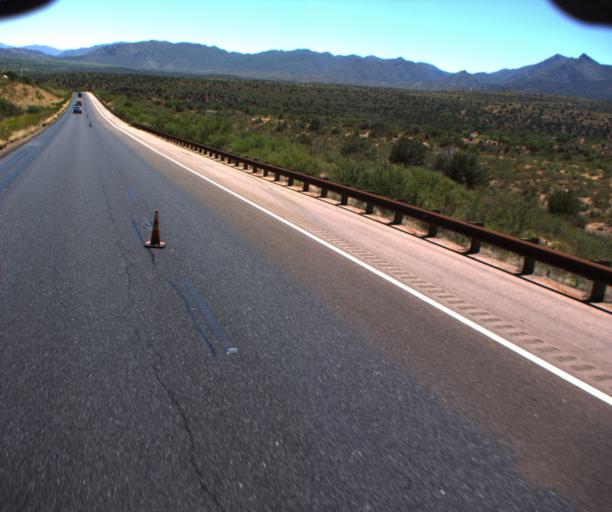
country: US
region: Arizona
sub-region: Gila County
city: Payson
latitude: 34.1245
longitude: -111.3568
